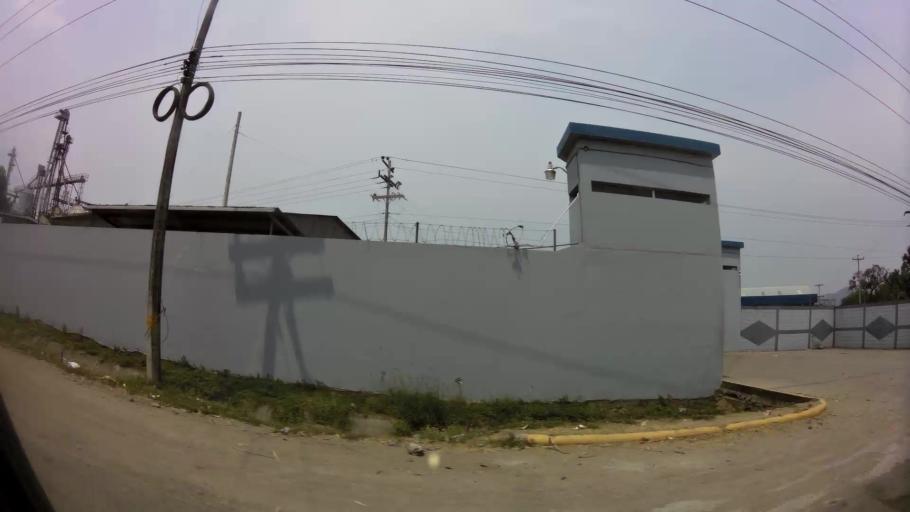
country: HN
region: Cortes
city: Villanueva
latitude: 15.3113
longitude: -87.9889
